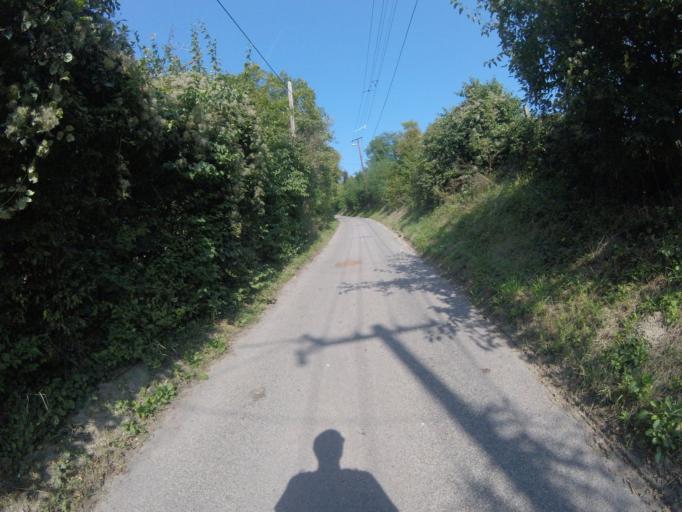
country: HU
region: Nograd
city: Bujak
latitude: 47.8856
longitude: 19.5361
